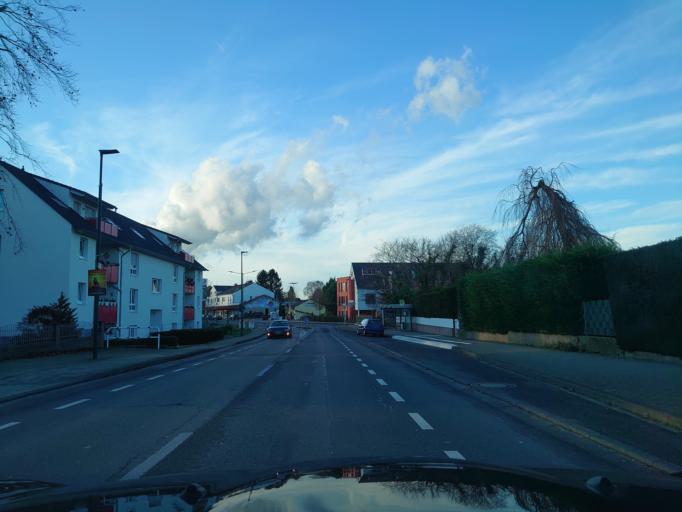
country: DE
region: North Rhine-Westphalia
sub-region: Regierungsbezirk Dusseldorf
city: Rommerskirchen
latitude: 51.0342
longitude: 6.6895
